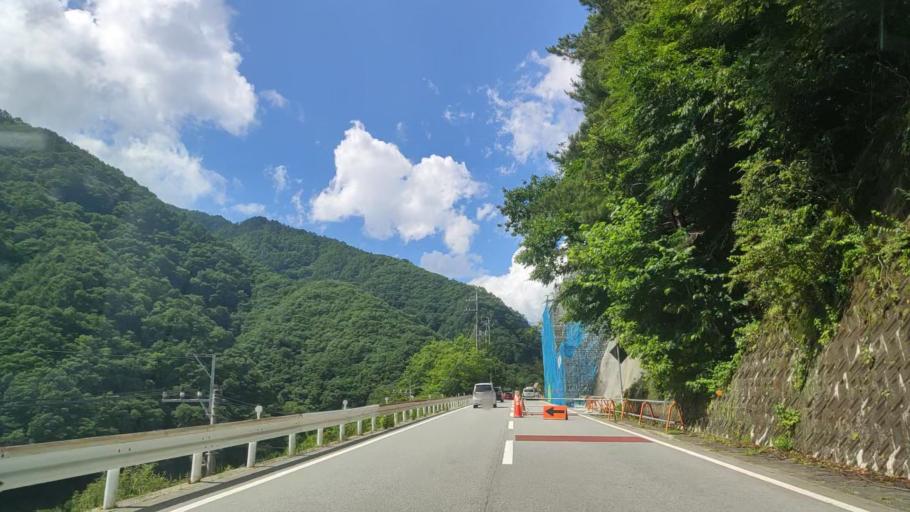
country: JP
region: Yamanashi
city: Enzan
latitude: 35.8306
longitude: 138.7646
